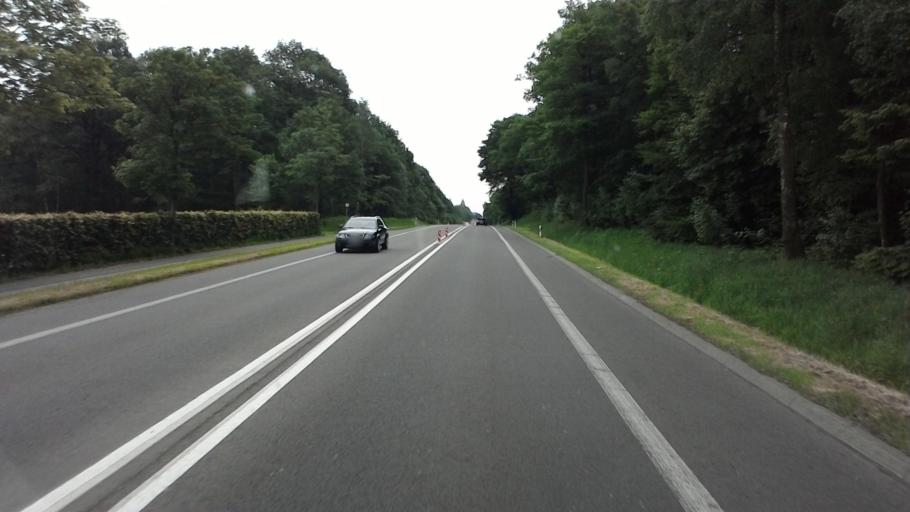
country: DE
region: North Rhine-Westphalia
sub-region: Regierungsbezirk Koln
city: Roetgen
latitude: 50.6314
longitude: 6.2198
